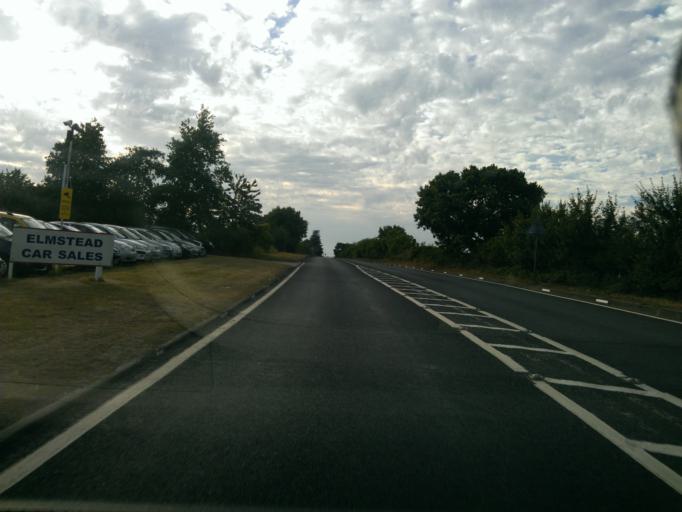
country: GB
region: England
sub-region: Essex
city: Alresford
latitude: 51.8725
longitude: 1.0120
